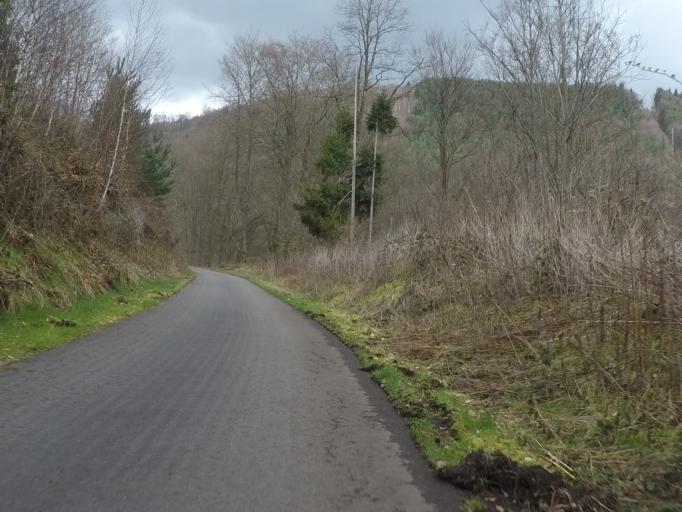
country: DE
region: Rheinland-Pfalz
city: Munchweiler an der Rodalbe
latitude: 49.2335
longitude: 7.6906
